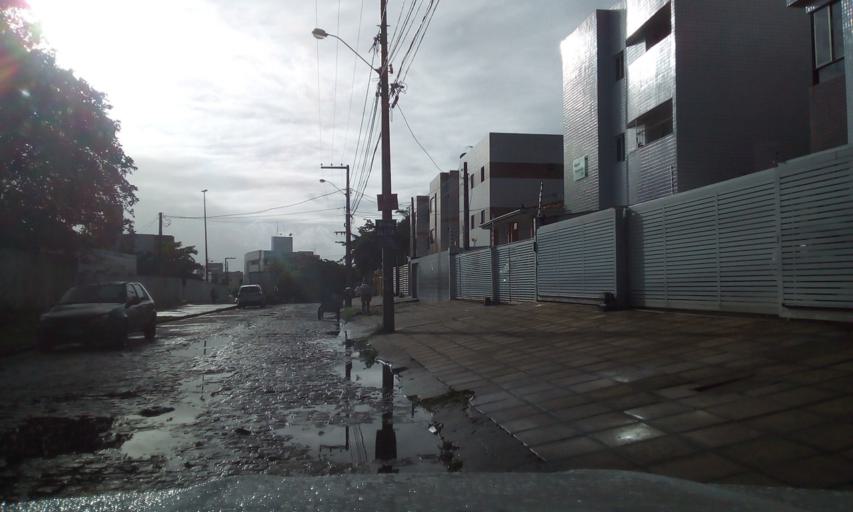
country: BR
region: Paraiba
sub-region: Joao Pessoa
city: Joao Pessoa
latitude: -7.1486
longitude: -34.8348
